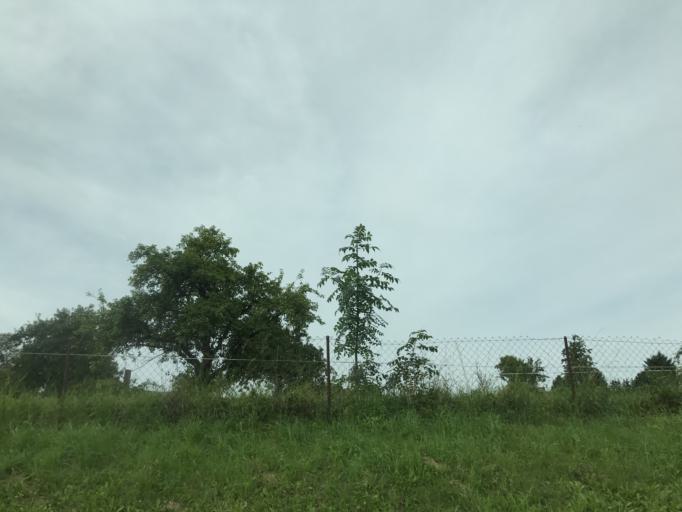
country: DE
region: Thuringia
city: Worbis
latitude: 51.4418
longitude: 10.3580
